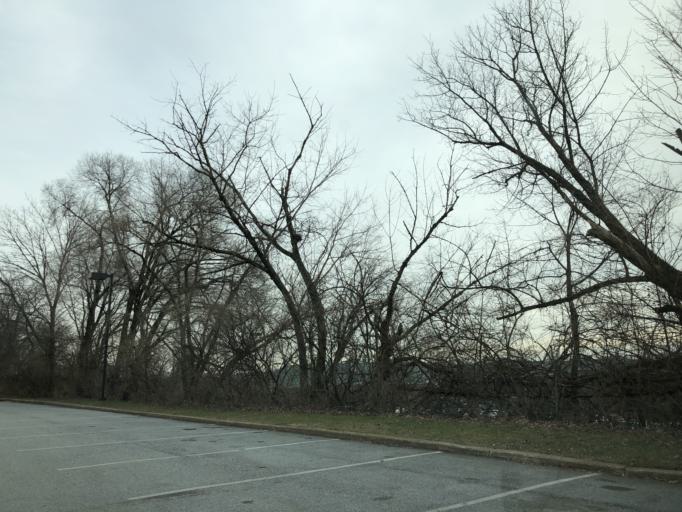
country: US
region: Pennsylvania
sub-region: Chester County
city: Exton
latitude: 40.0335
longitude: -75.6250
